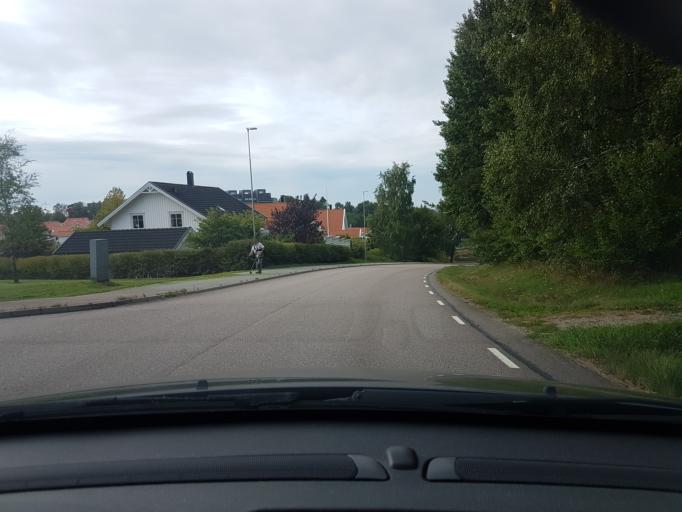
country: SE
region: Vaestra Goetaland
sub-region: Ale Kommun
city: Surte
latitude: 57.8506
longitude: 12.0334
